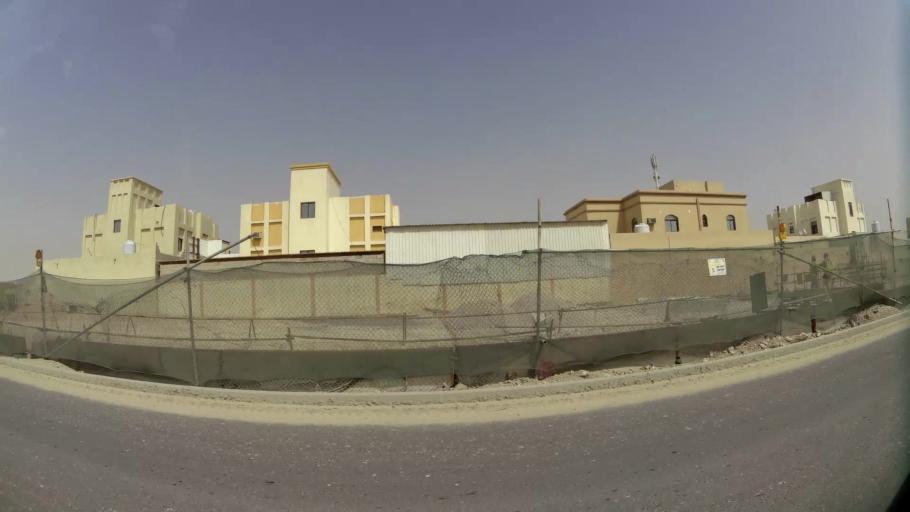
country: QA
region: Baladiyat ar Rayyan
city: Ar Rayyan
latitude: 25.2469
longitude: 51.3622
